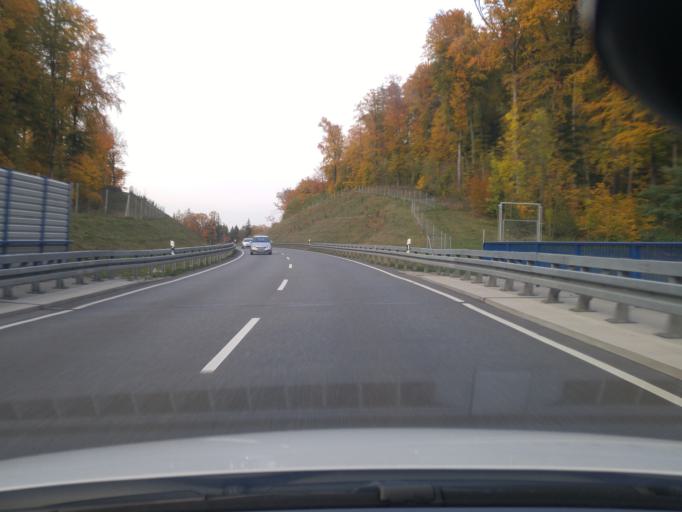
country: DE
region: Baden-Wuerttemberg
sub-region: Karlsruhe Region
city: Muhlhausen
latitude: 49.2398
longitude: 8.7283
